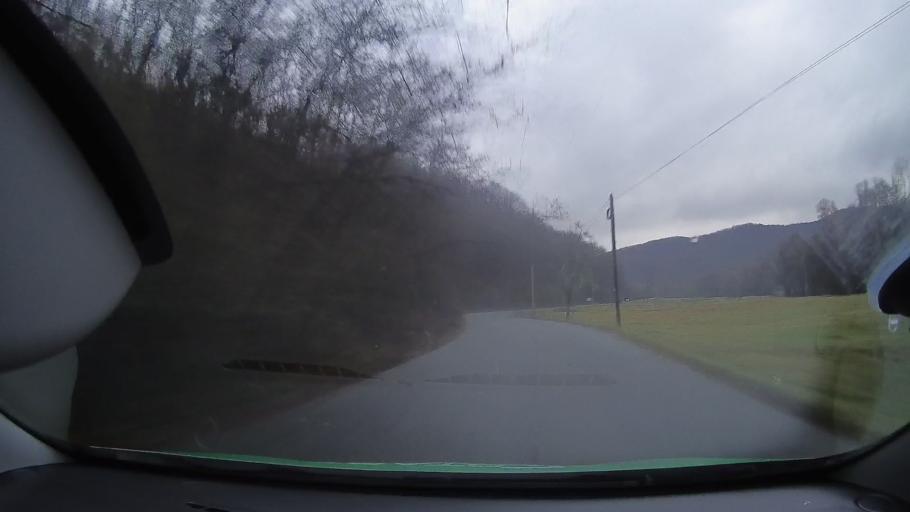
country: RO
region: Hunedoara
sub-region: Comuna Baia de Cris
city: Baia de Cris
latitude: 46.2015
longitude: 22.7181
